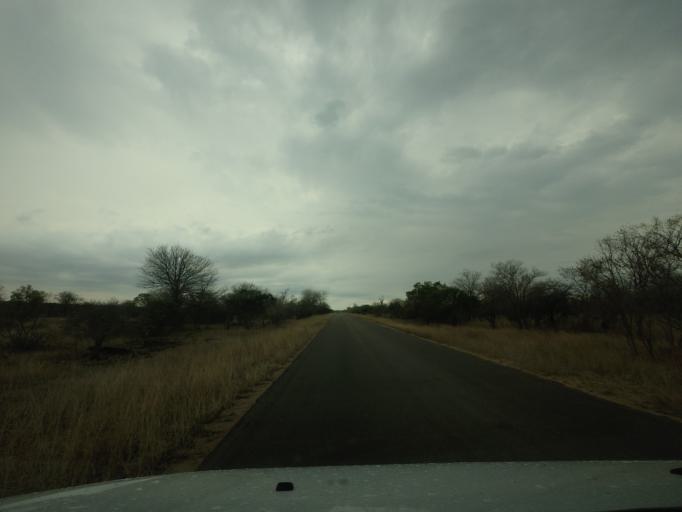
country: ZA
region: Limpopo
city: Thulamahashi
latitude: -24.4716
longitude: 31.4298
